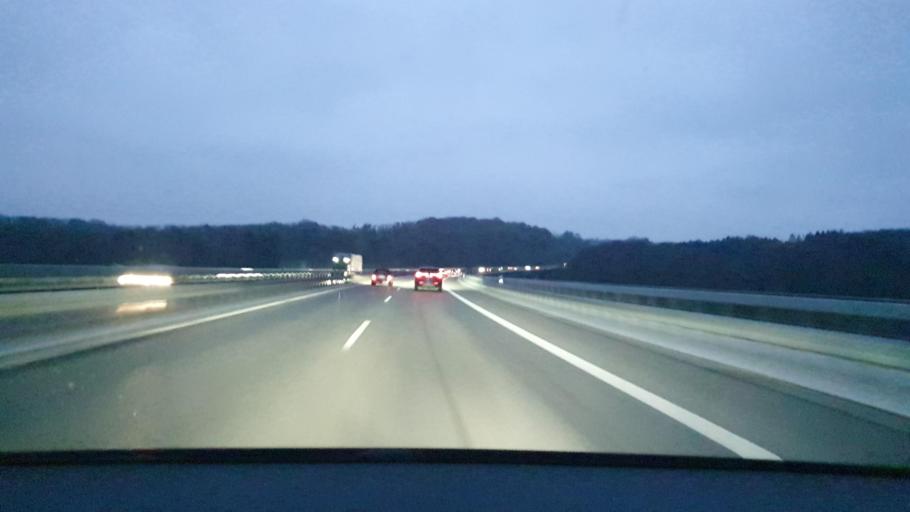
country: DE
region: Baden-Wuerttemberg
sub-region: Regierungsbezirk Stuttgart
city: Schlaitdorf
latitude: 48.6217
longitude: 9.2263
